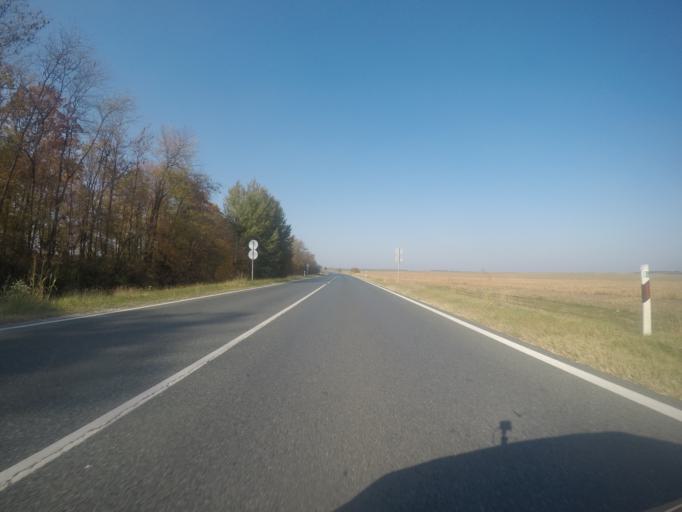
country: HU
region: Tolna
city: Madocsa
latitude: 46.7056
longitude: 18.8884
